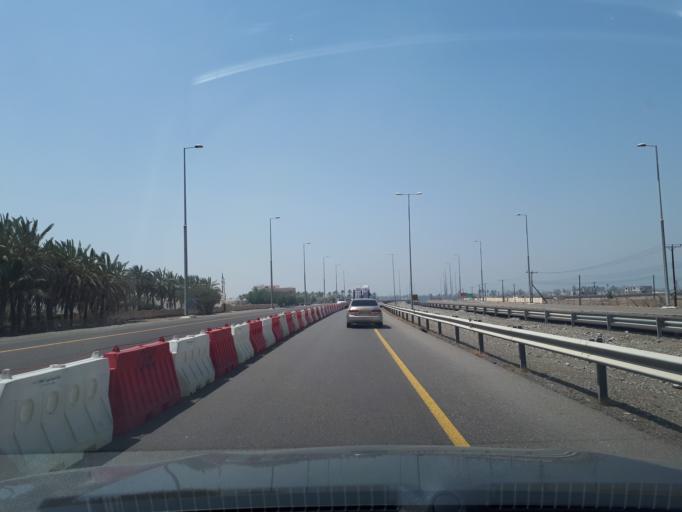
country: OM
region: Al Batinah
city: Al Liwa'
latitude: 24.5933
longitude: 56.5302
